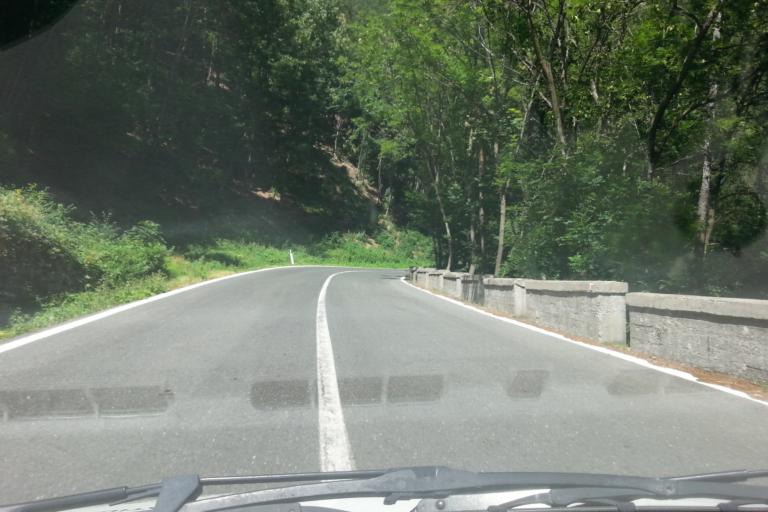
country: IT
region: Piedmont
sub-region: Provincia di Torino
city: Venaus
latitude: 45.1535
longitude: 6.9949
